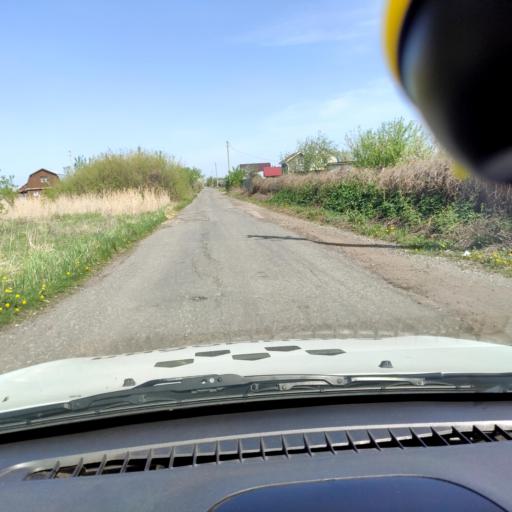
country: RU
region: Samara
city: Tol'yatti
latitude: 53.6660
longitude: 49.3626
